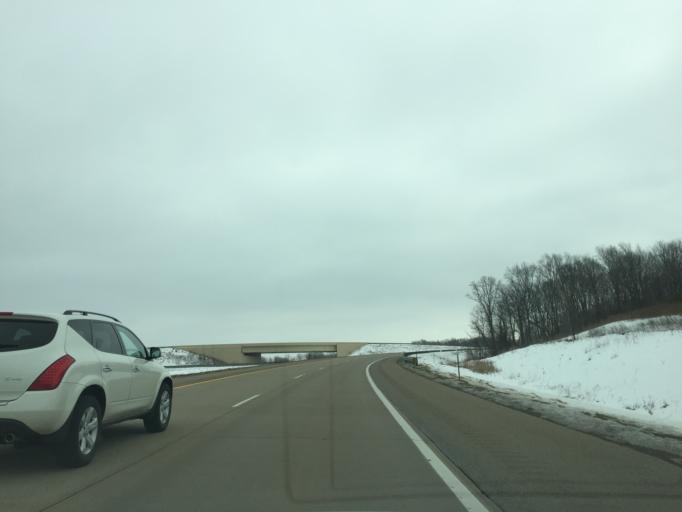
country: US
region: Michigan
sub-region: Ottawa County
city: Hudsonville
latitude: 42.8609
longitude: -85.8203
